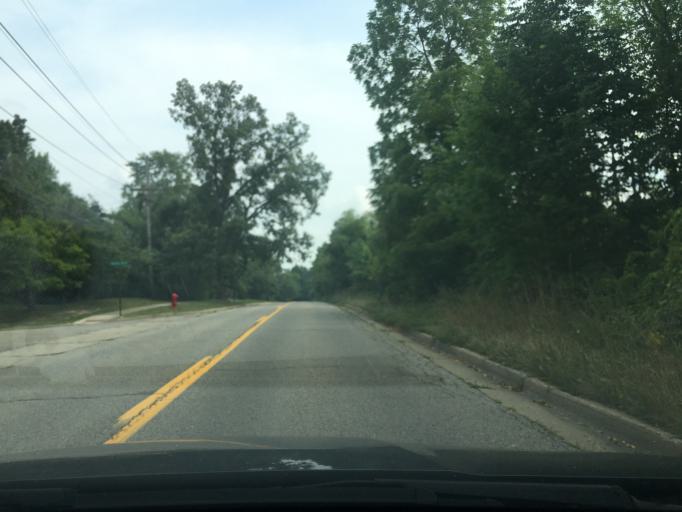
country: US
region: Michigan
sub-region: Oakland County
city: Birmingham
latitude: 42.5632
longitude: -83.2120
